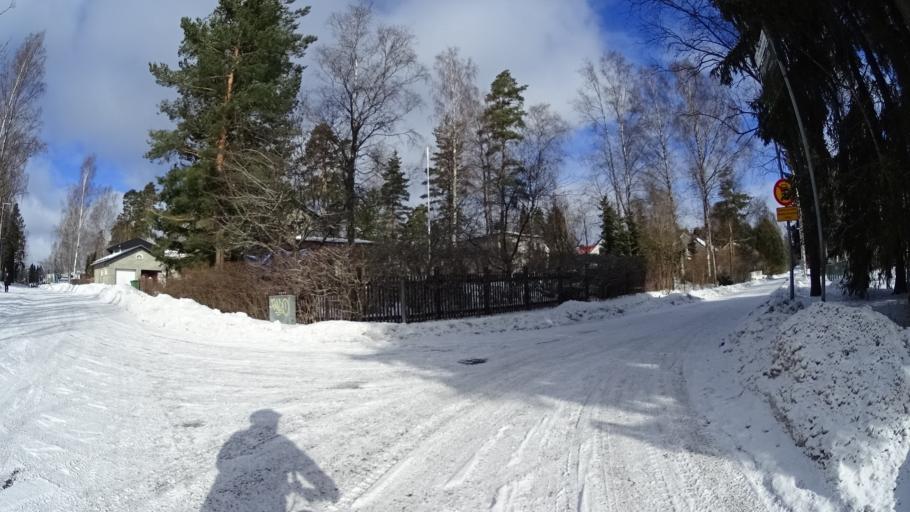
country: FI
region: Uusimaa
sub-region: Helsinki
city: Kilo
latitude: 60.2582
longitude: 24.8229
